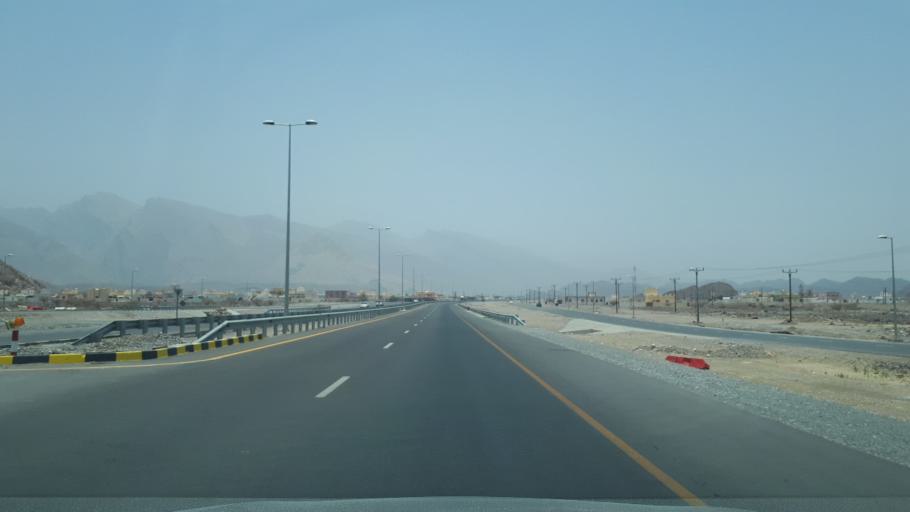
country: OM
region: Al Batinah
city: Rustaq
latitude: 23.4226
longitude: 57.3719
